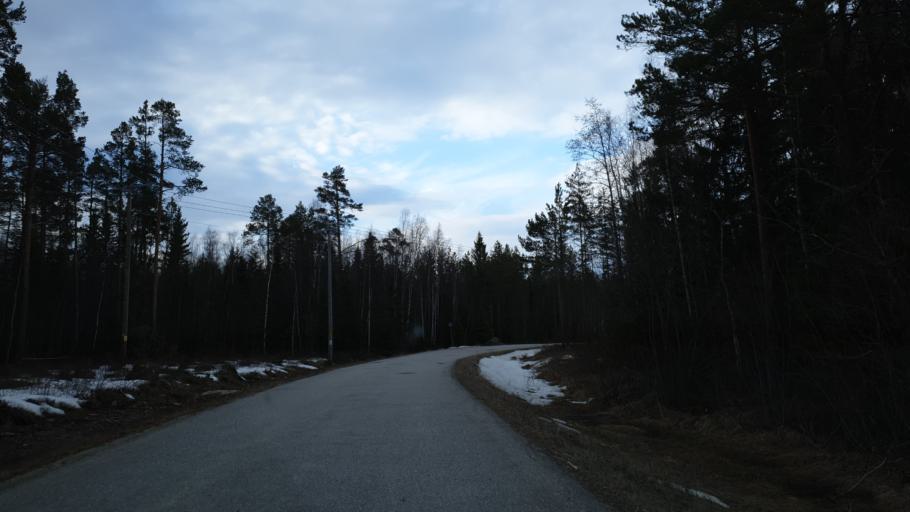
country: SE
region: Vaesternorrland
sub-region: Sundsvalls Kommun
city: Njurundabommen
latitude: 61.9890
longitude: 17.3771
